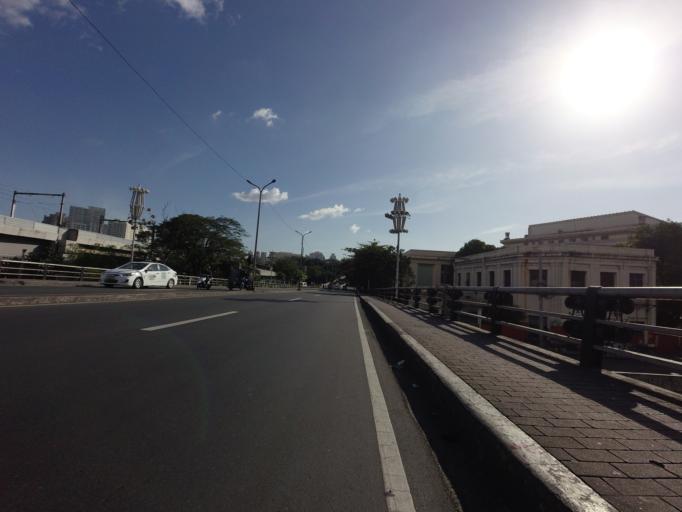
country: PH
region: Metro Manila
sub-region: City of Manila
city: Quiapo
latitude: 14.5965
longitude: 120.9803
